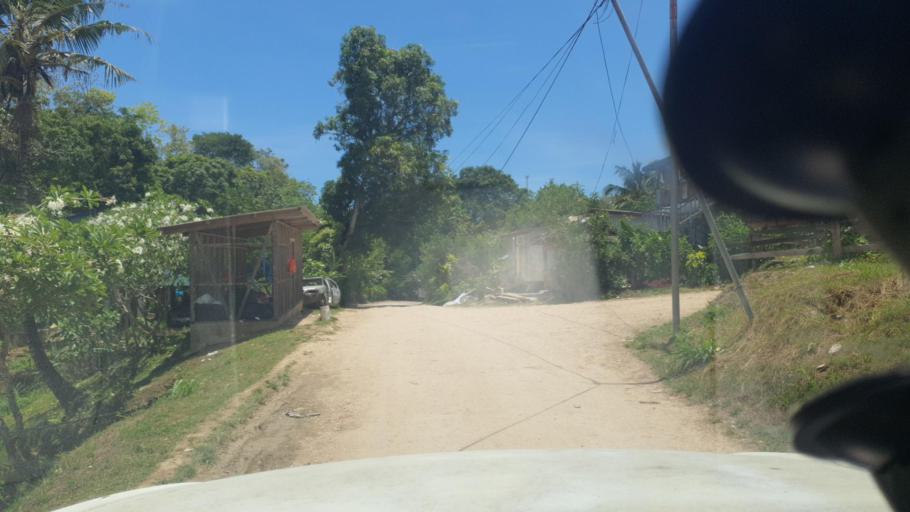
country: SB
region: Guadalcanal
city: Honiara
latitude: -9.4318
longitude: 159.9358
